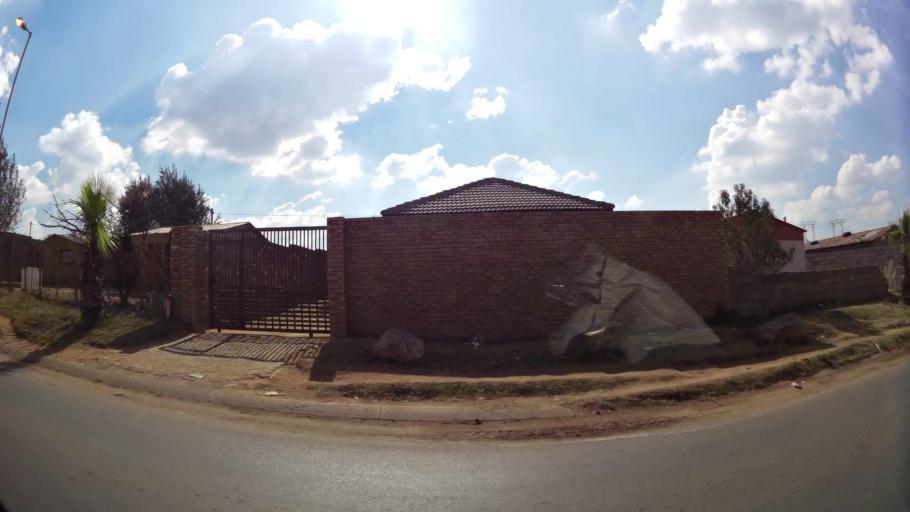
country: ZA
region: Gauteng
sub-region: City of Johannesburg Metropolitan Municipality
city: Roodepoort
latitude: -26.1900
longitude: 27.8638
